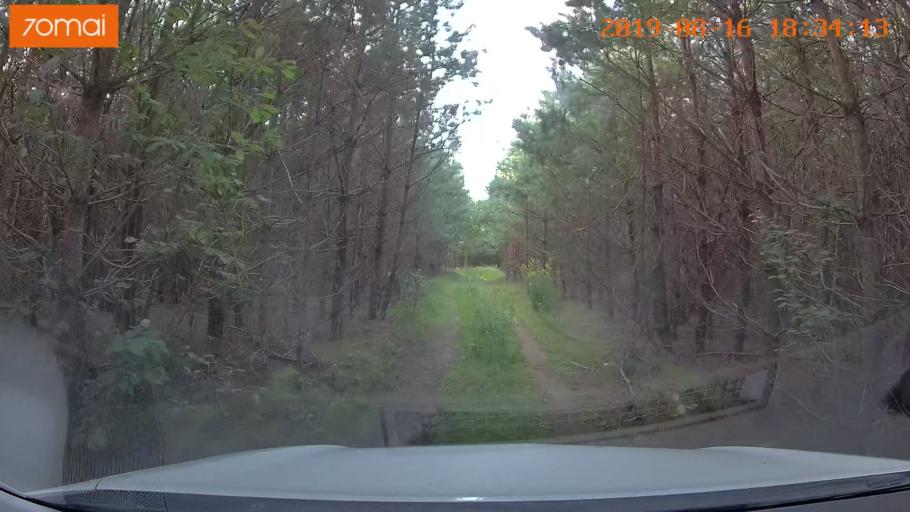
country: BY
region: Mogilev
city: Asipovichy
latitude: 53.2029
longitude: 28.6388
